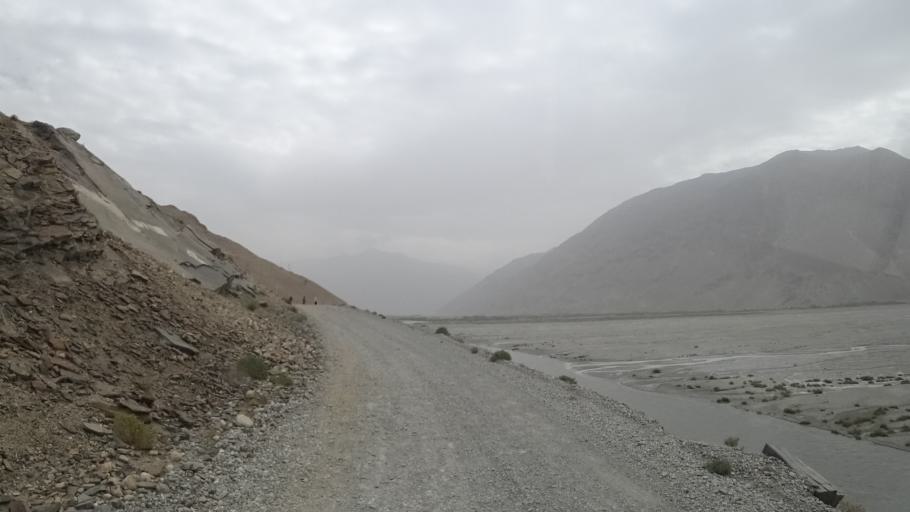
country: AF
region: Badakhshan
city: Khandud
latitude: 37.0031
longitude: 72.5481
